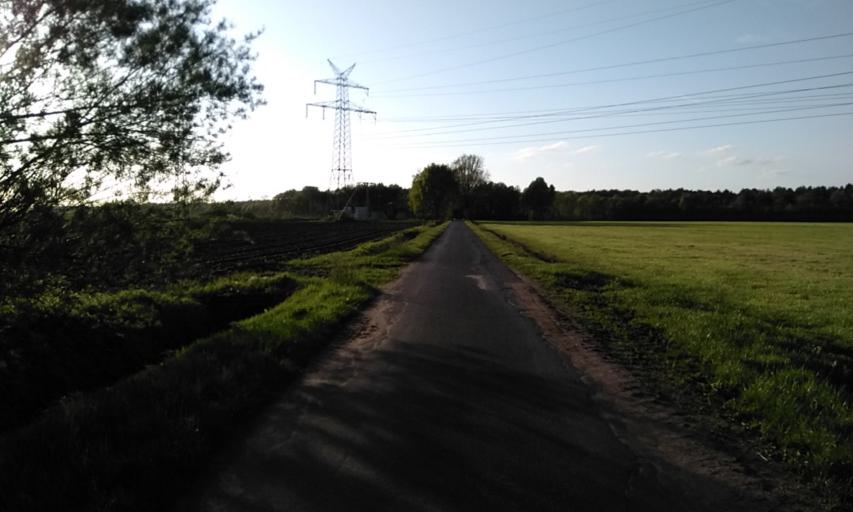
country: DE
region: Lower Saxony
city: Harsefeld
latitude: 53.4086
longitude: 9.5057
